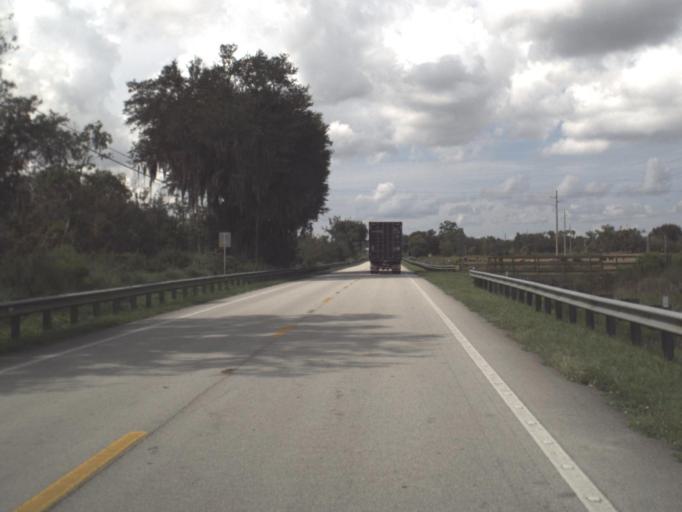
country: US
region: Florida
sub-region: Highlands County
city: Lake Placid
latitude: 27.2084
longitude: -81.2790
